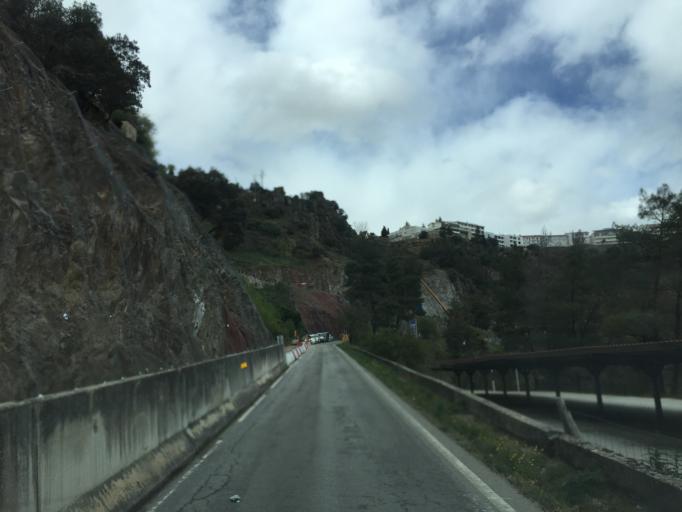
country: PT
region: Braganca
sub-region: Miranda do Douro
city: Miranda do Douro
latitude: 41.4930
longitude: -6.2694
